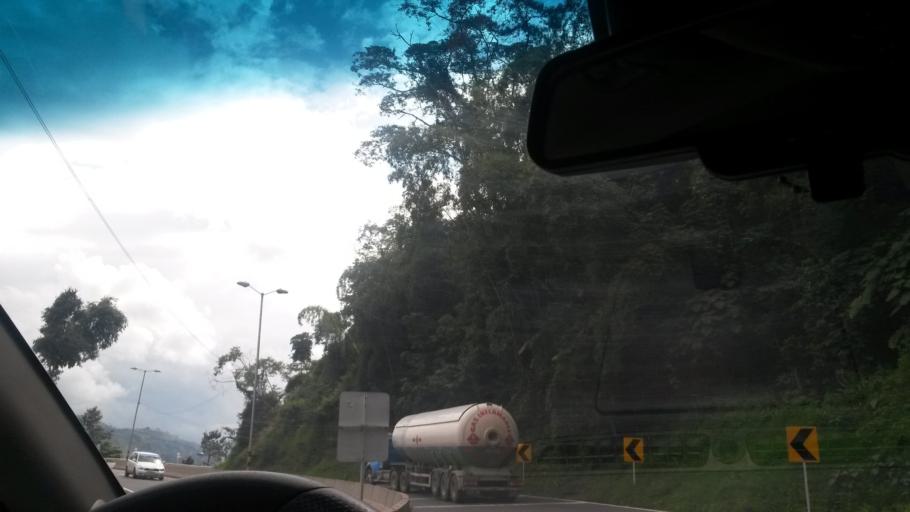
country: CO
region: Caldas
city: Manizales
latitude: 5.0529
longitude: -75.5651
